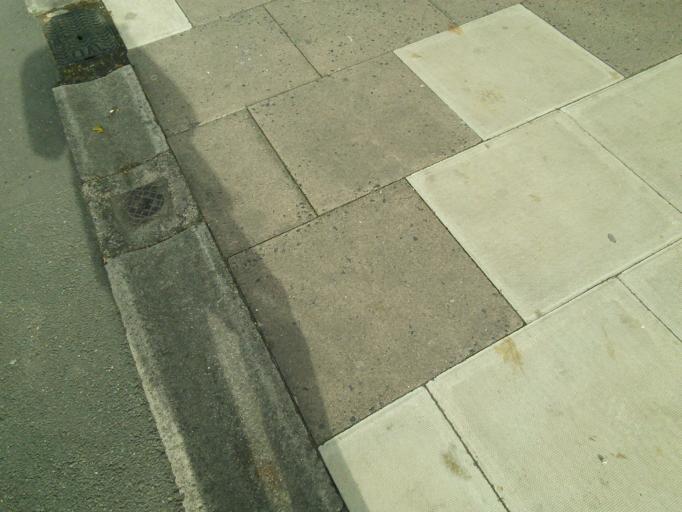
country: GB
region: England
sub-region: City and Borough of Birmingham
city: Bartley Green
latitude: 52.4384
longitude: -1.9397
